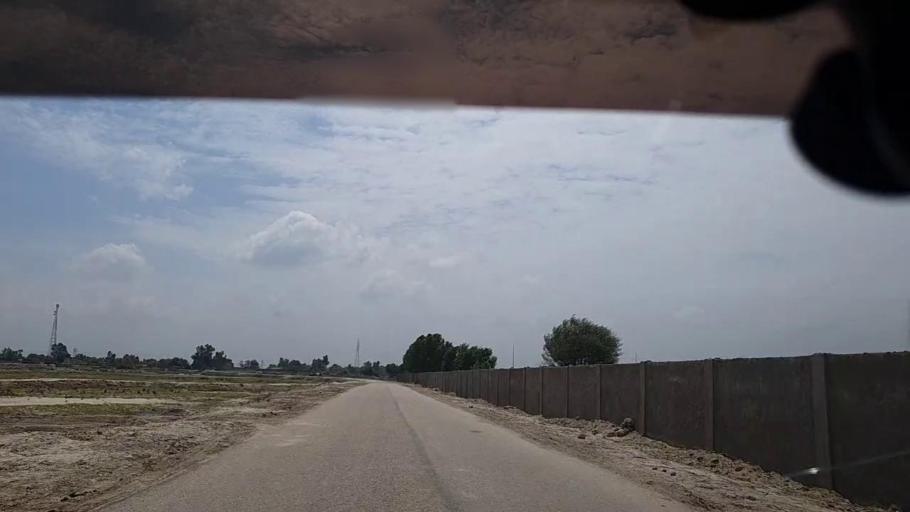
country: PK
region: Sindh
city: Ghauspur
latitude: 28.0925
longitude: 68.9598
